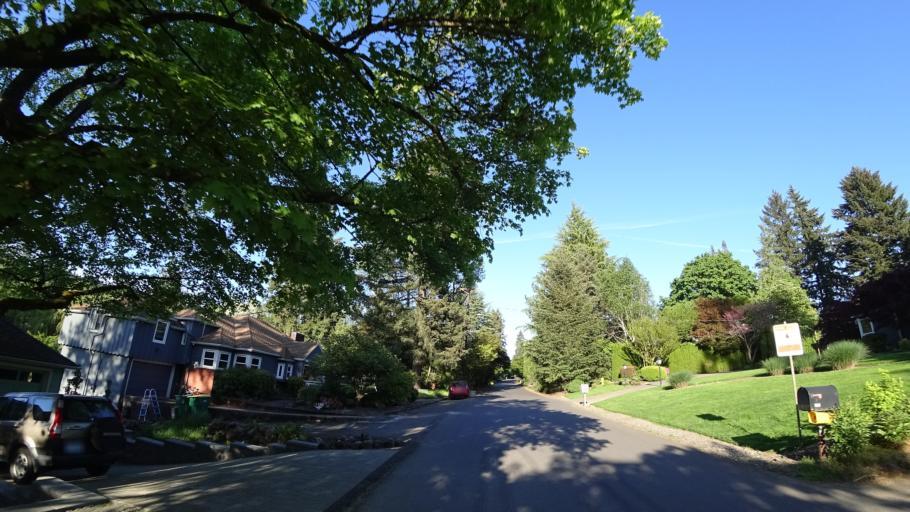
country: US
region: Oregon
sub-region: Washington County
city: West Slope
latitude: 45.4932
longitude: -122.7618
